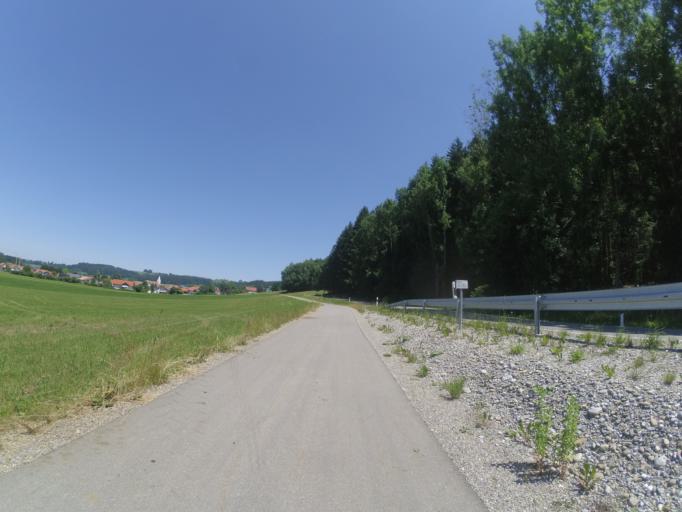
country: DE
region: Bavaria
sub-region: Swabia
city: Untrasried
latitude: 47.8496
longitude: 10.3528
